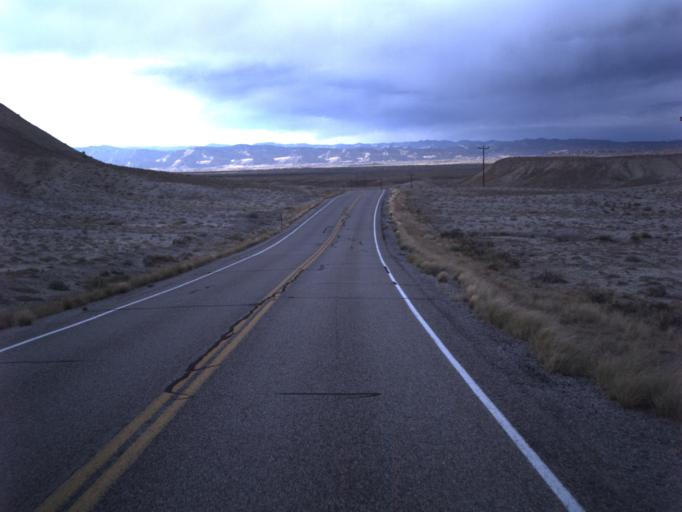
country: US
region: Utah
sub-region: Grand County
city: Moab
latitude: 38.9323
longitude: -109.3445
